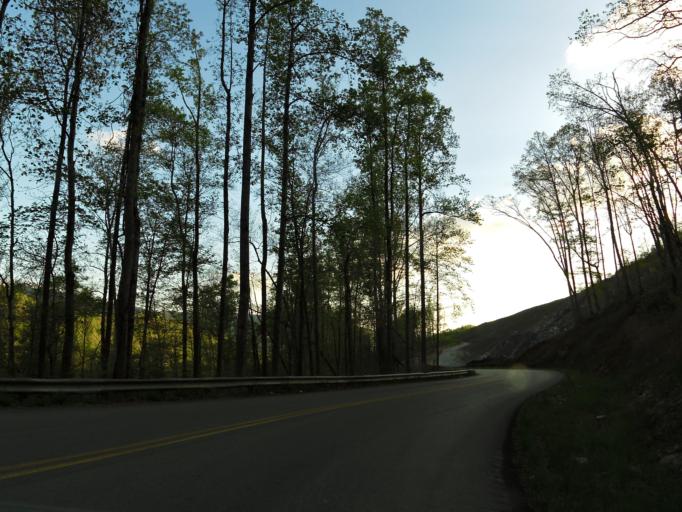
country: US
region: Kentucky
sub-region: Bell County
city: Middlesboro
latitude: 36.6104
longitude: -83.8771
